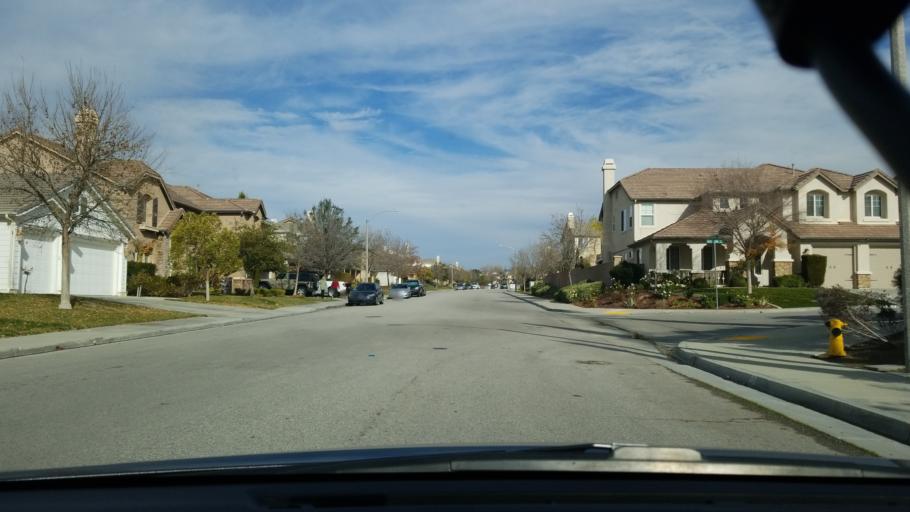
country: US
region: California
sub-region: Riverside County
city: Temecula
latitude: 33.4686
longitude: -117.0658
